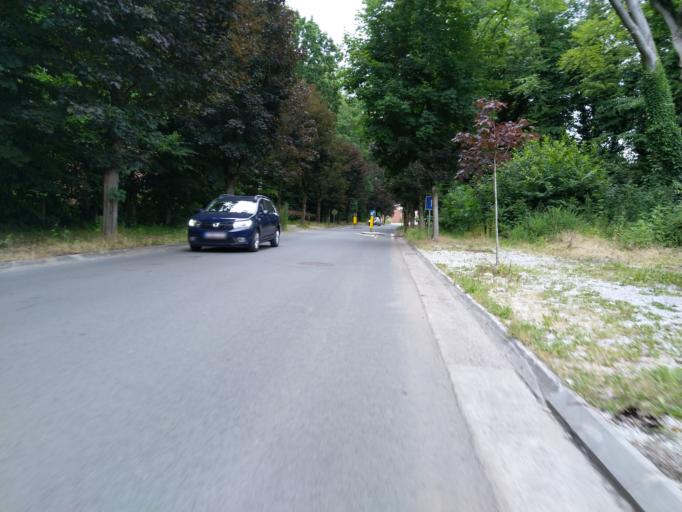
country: BE
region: Wallonia
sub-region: Province du Hainaut
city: Mons
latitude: 50.4639
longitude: 3.9972
